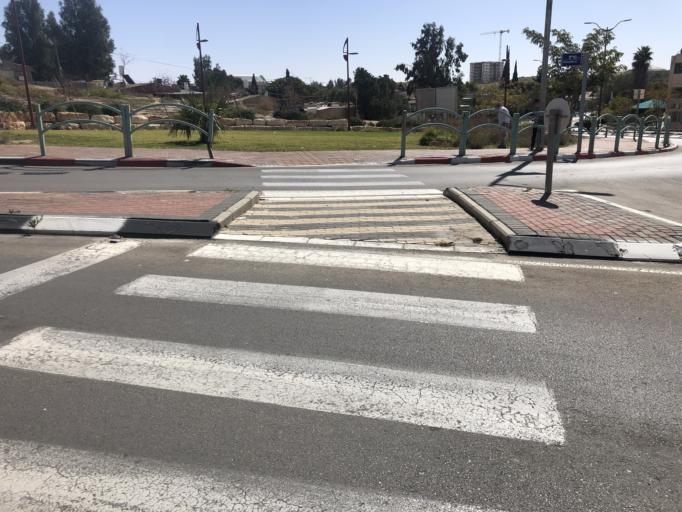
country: IL
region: Southern District
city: Dimona
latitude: 31.0686
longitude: 35.0399
